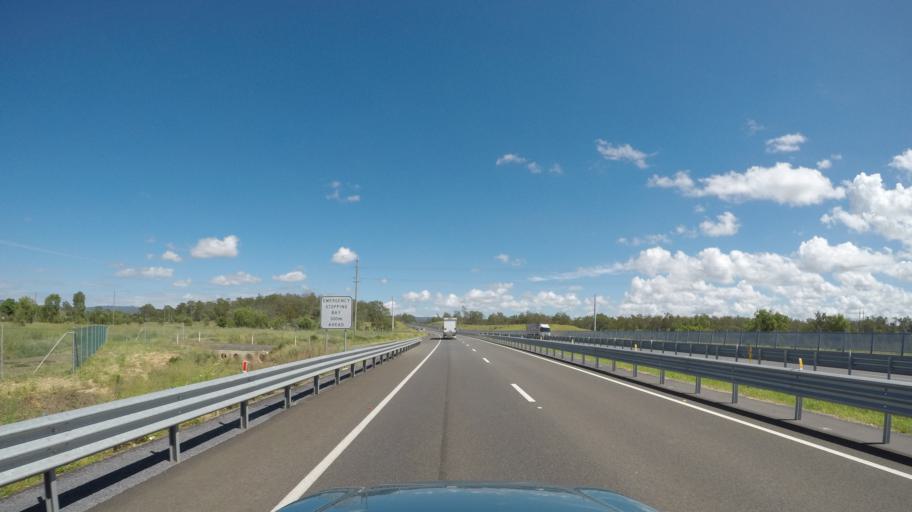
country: AU
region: Queensland
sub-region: Toowoomba
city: Rangeville
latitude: -27.5320
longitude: 152.0740
